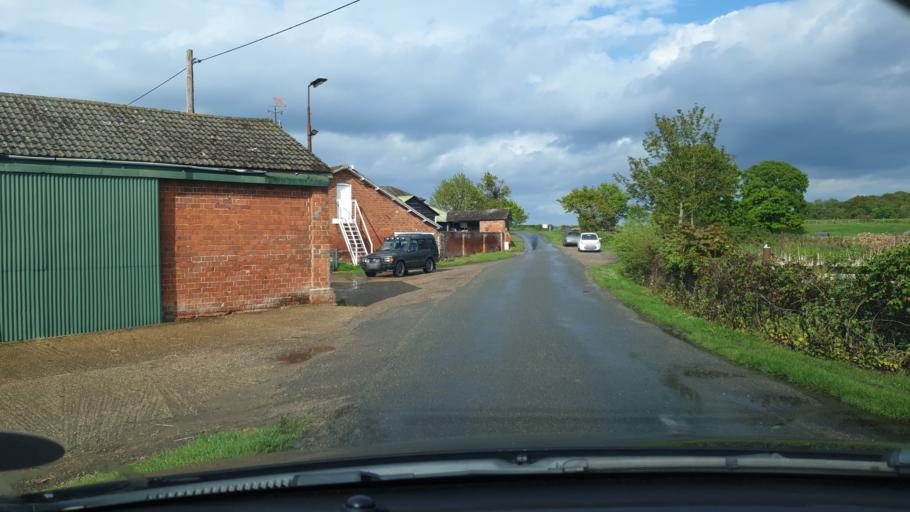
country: GB
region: England
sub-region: Essex
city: Saint Osyth
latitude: 51.8219
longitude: 1.0765
